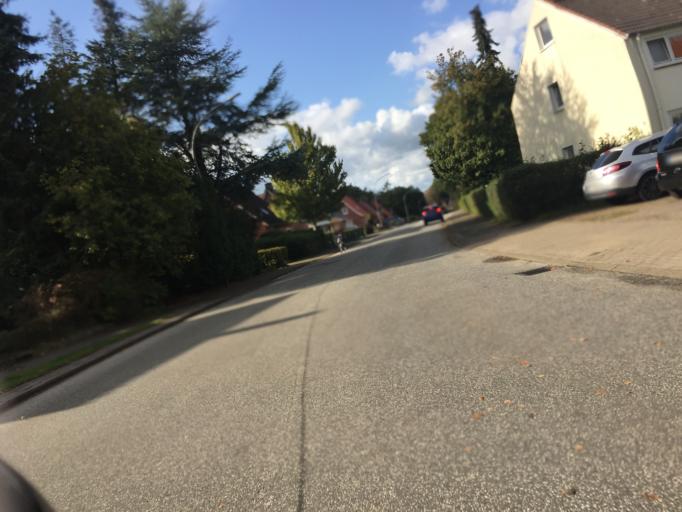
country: DE
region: Schleswig-Holstein
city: Ottenbuttel
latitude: 53.9512
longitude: 9.5051
